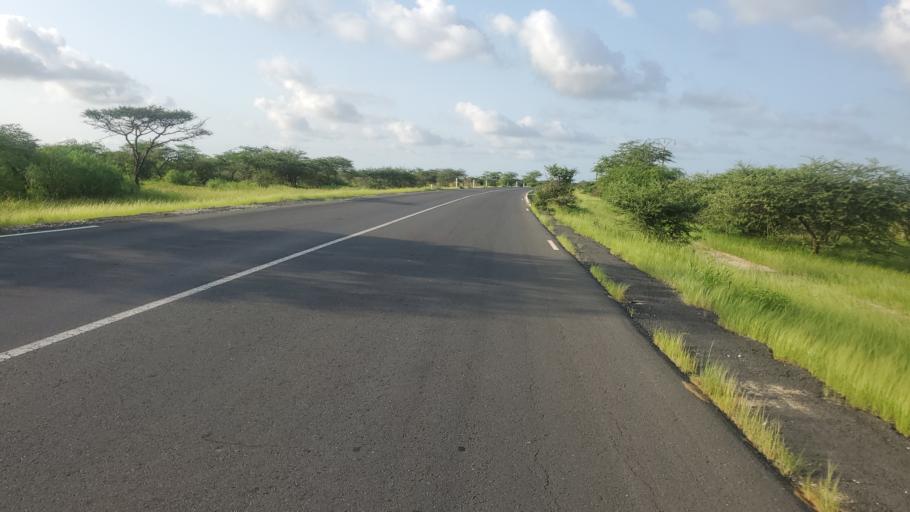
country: SN
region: Saint-Louis
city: Saint-Louis
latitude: 16.1195
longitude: -16.4142
